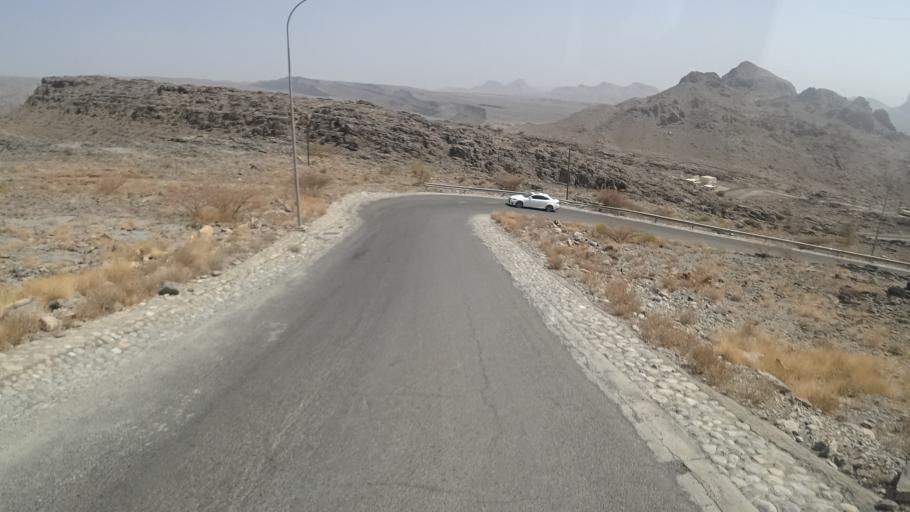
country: OM
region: Muhafazat ad Dakhiliyah
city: Bahla'
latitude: 23.1323
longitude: 57.3056
